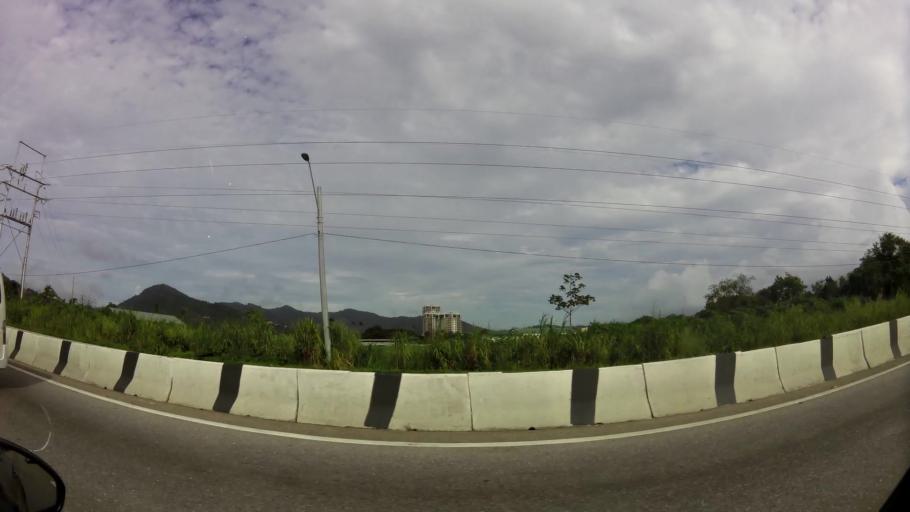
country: TT
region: City of Port of Spain
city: Mucurapo
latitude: 10.6667
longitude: -61.5364
